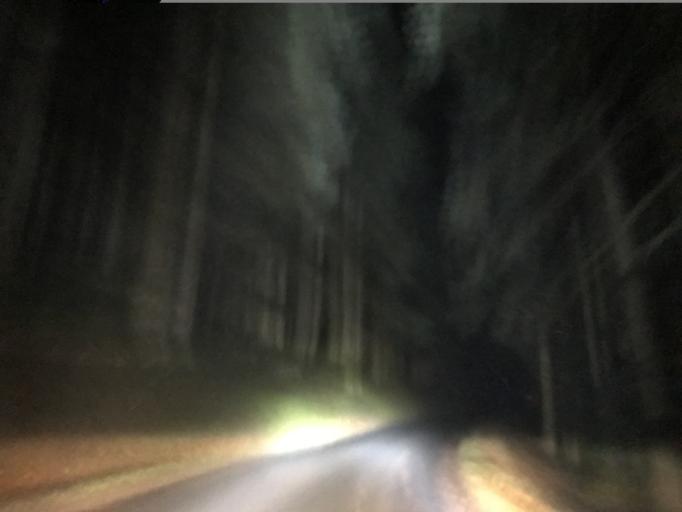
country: FR
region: Auvergne
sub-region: Departement du Puy-de-Dome
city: Saint-Remy-sur-Durolle
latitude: 45.9438
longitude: 3.6364
